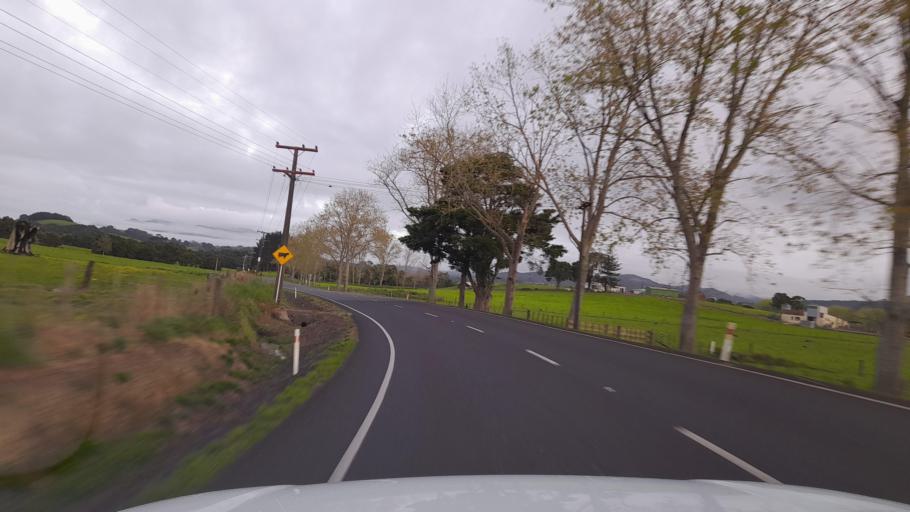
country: NZ
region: Northland
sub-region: Whangarei
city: Maungatapere
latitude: -35.7285
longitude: 174.0465
